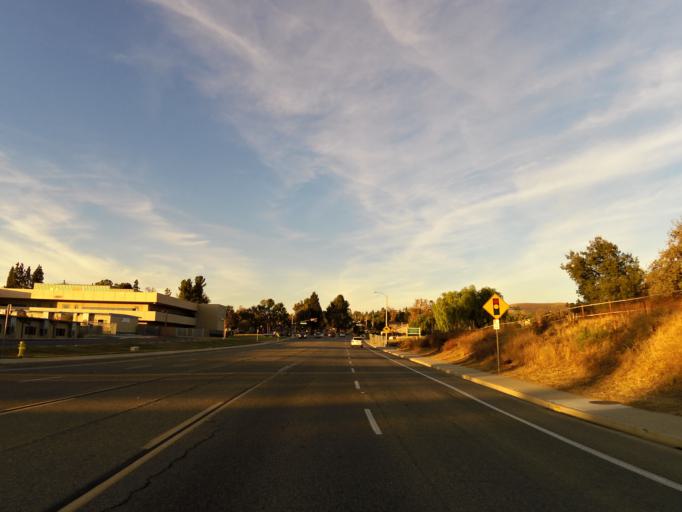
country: US
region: California
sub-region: Ventura County
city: Thousand Oaks
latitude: 34.2060
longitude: -118.8396
